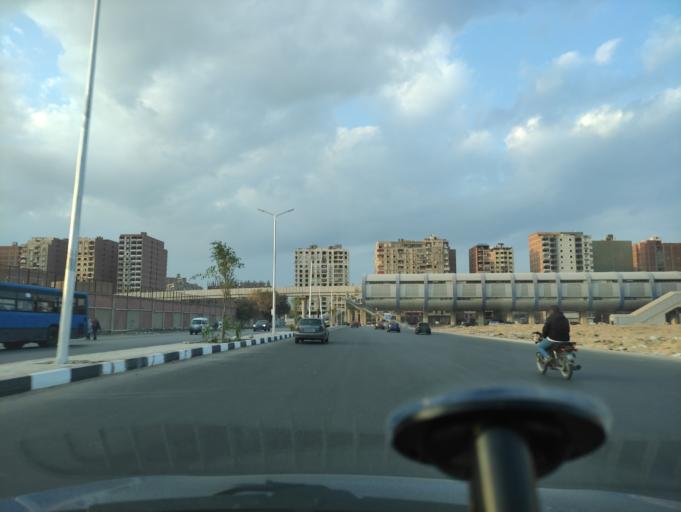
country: EG
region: Muhafazat al Qalyubiyah
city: Al Khankah
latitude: 30.1259
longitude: 31.3604
